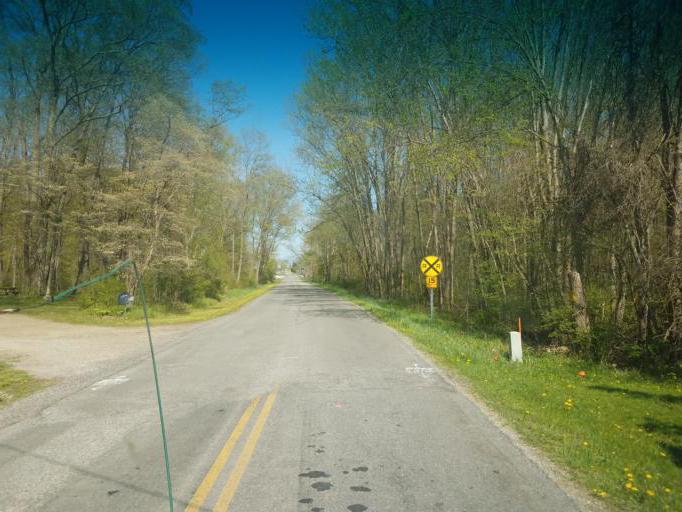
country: US
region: Ohio
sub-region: Medina County
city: Westfield Center
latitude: 40.9976
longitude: -81.9660
